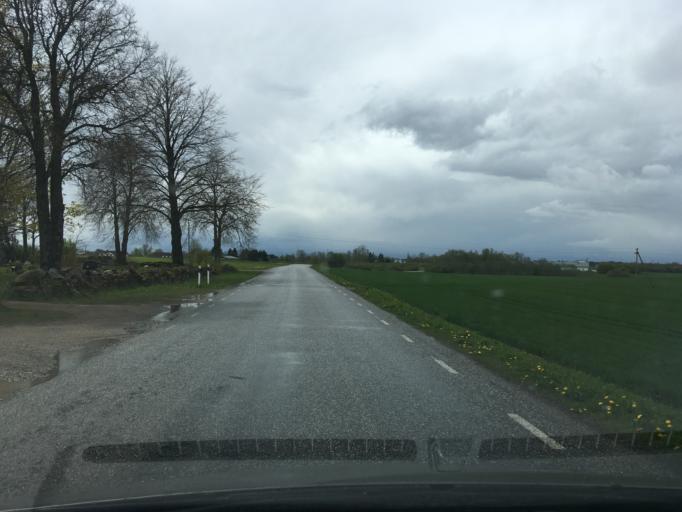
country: EE
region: Harju
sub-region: Joelaehtme vald
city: Loo
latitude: 59.4217
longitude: 24.9822
